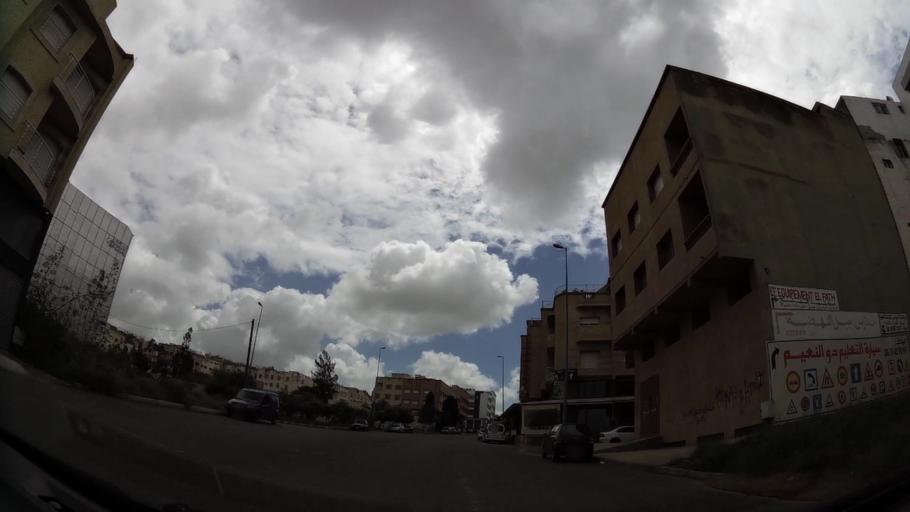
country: MA
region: Grand Casablanca
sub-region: Casablanca
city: Casablanca
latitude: 33.5347
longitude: -7.5898
